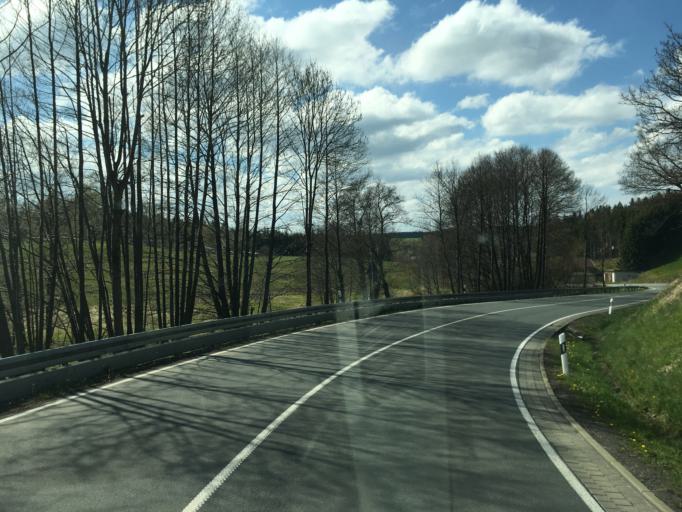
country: DE
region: Saxony-Anhalt
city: Hasselfelde
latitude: 51.6842
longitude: 10.7926
